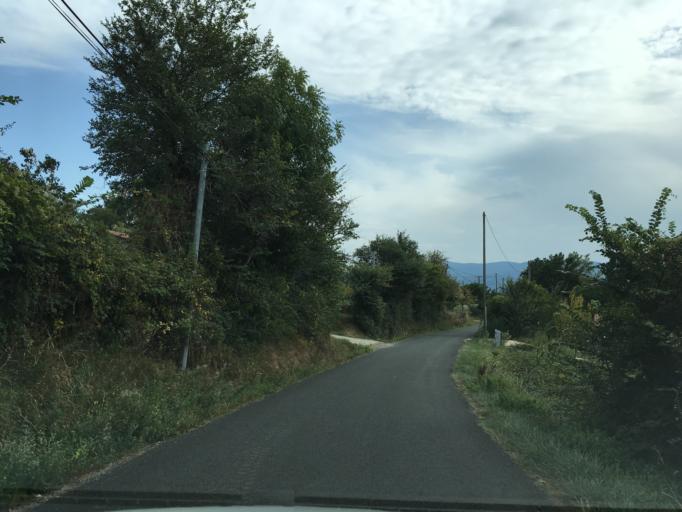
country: FR
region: Midi-Pyrenees
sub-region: Departement du Tarn
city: Lagarrigue
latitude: 43.5994
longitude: 2.2890
